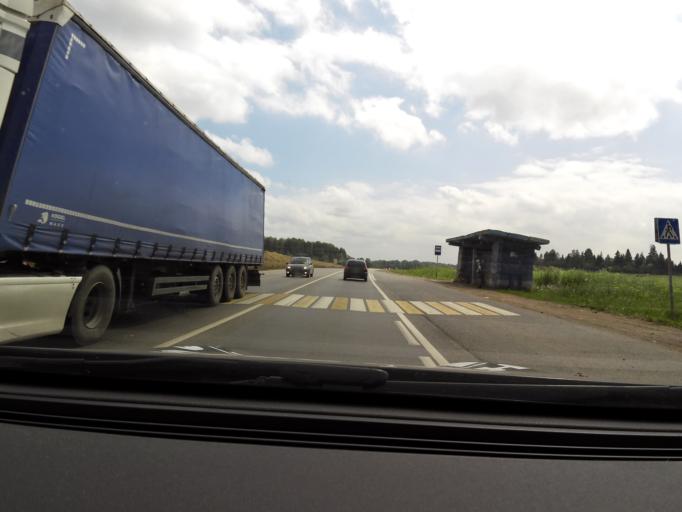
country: RU
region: Perm
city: Bershet'
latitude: 57.6814
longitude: 56.4265
